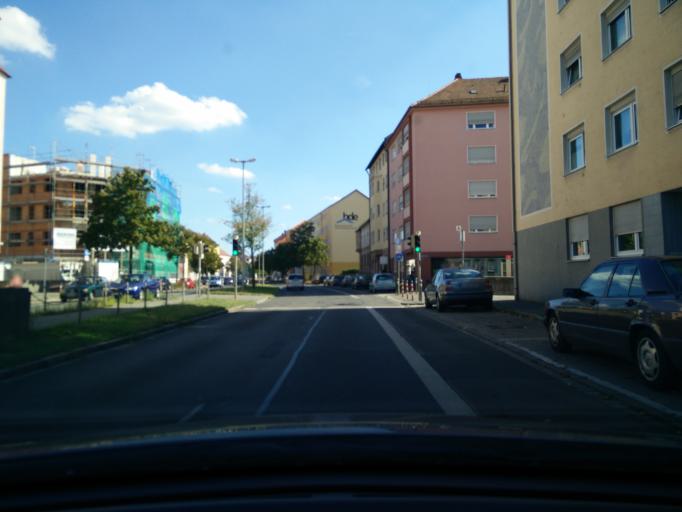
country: DE
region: Bavaria
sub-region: Regierungsbezirk Mittelfranken
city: Nuernberg
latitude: 49.4354
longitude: 11.0841
